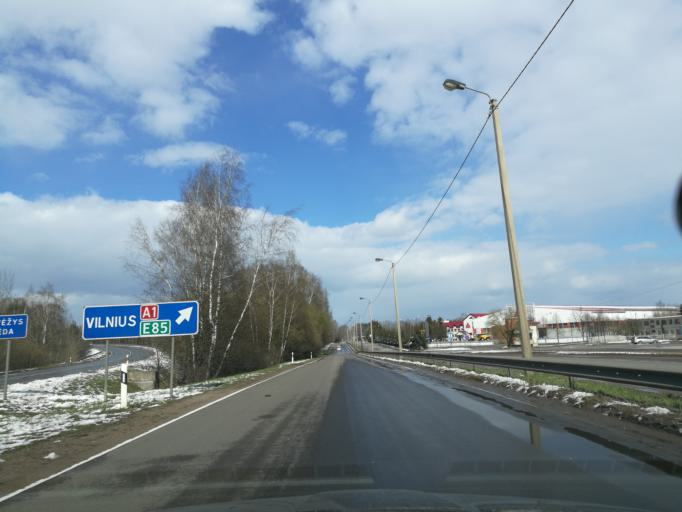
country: LT
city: Ramuciai
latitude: 54.9235
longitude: 24.0493
